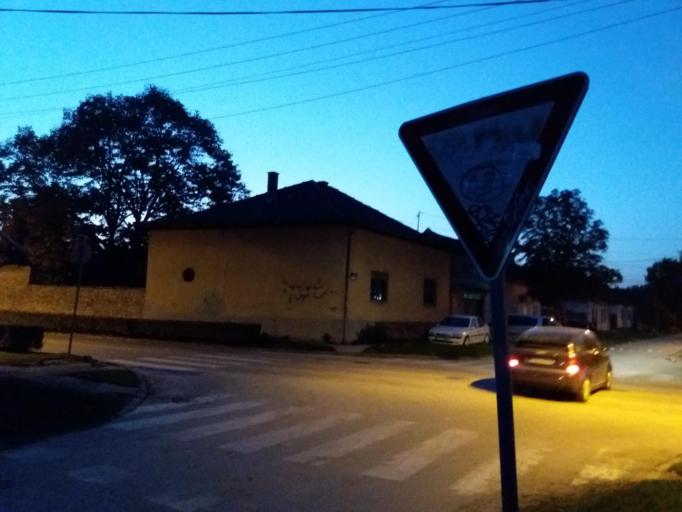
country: RS
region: Autonomna Pokrajina Vojvodina
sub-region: Severnobacki Okrug
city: Subotica
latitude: 46.0915
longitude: 19.6681
